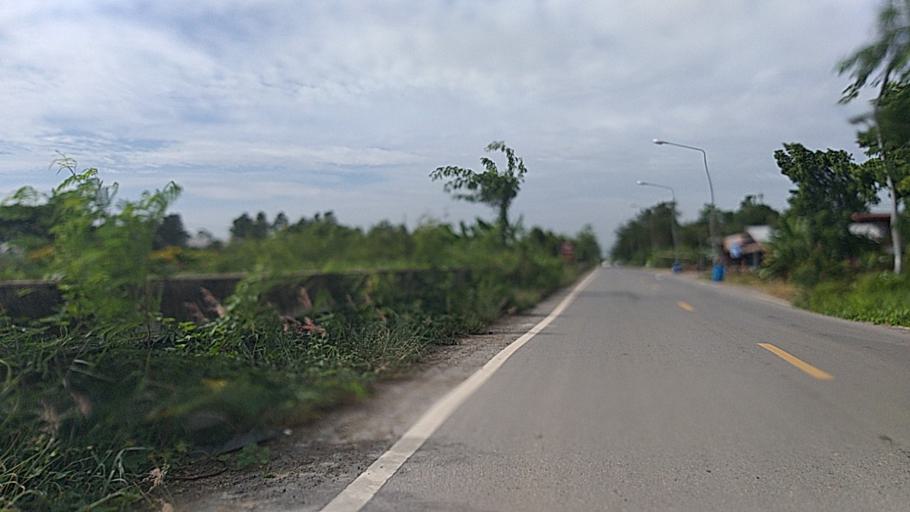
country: TH
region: Pathum Thani
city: Nong Suea
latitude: 14.0534
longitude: 100.8927
